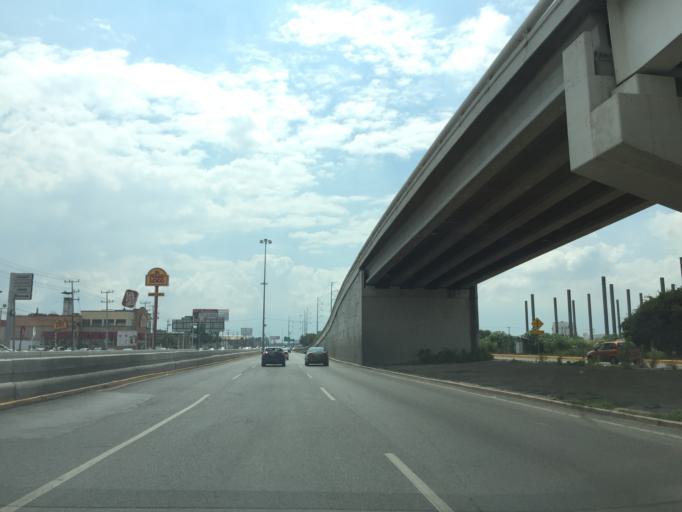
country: MX
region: Nuevo Leon
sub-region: San Nicolas de los Garza
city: San Nicolas de los Garza
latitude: 25.7652
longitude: -100.3054
